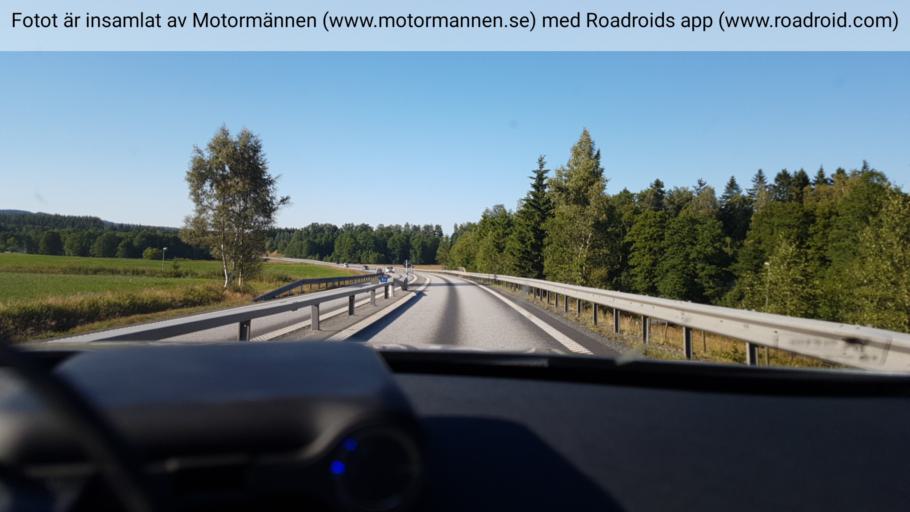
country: SE
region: Joenkoeping
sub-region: Jonkopings Kommun
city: Bankeryd
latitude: 57.8413
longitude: 14.1068
